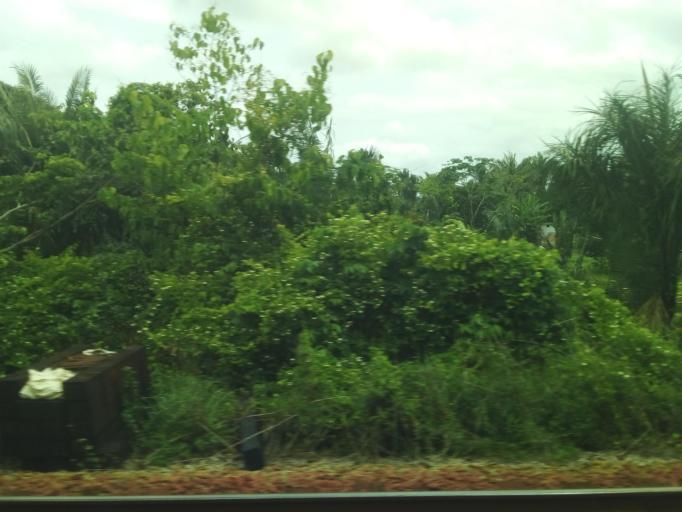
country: BR
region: Maranhao
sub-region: Arari
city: Arari
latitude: -3.5696
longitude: -44.7766
